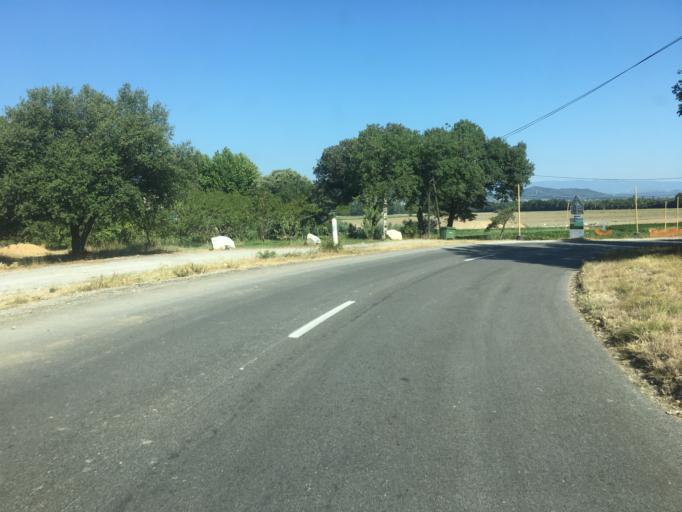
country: FR
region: Provence-Alpes-Cote d'Azur
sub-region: Departement des Alpes-de-Haute-Provence
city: Volx
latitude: 43.8490
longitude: 5.8791
